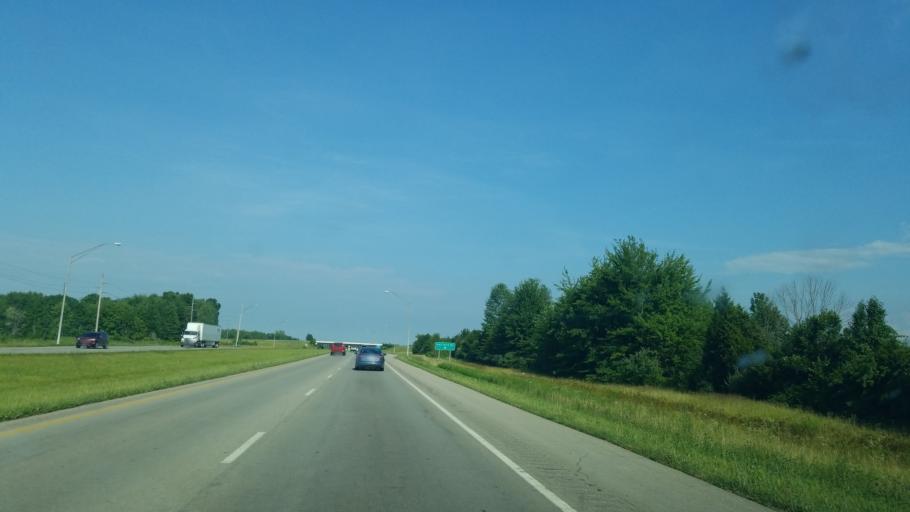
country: US
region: Ohio
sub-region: Clermont County
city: Williamsburg
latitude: 39.0710
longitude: -84.1007
